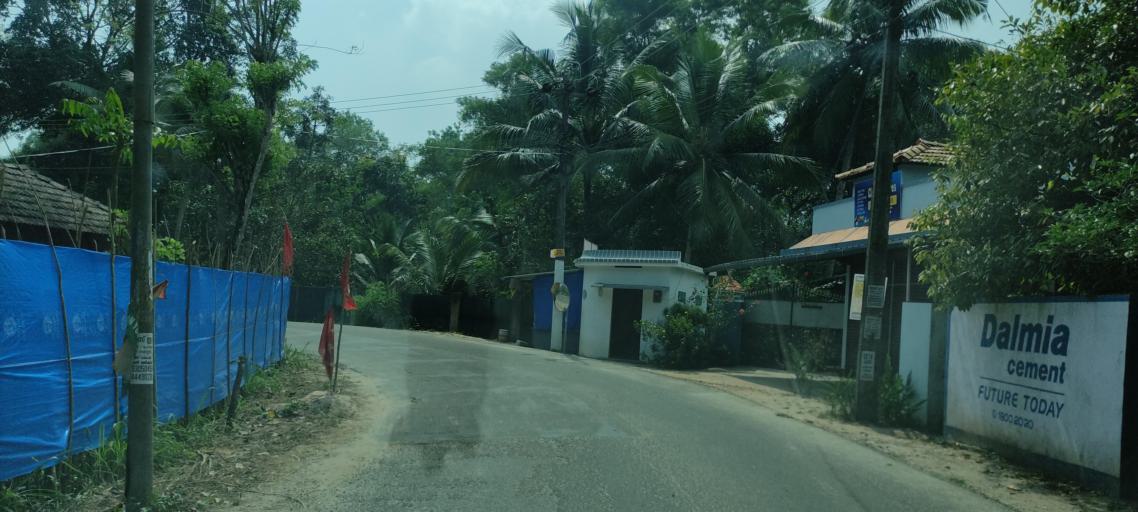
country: IN
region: Kerala
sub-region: Alappuzha
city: Shertallai
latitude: 9.6138
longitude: 76.3470
